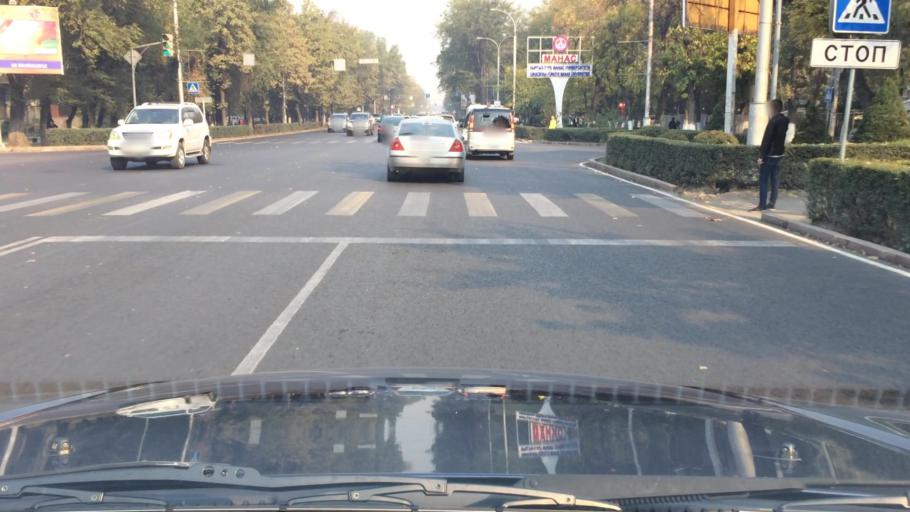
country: KG
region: Chuy
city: Bishkek
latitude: 42.8481
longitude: 74.5863
